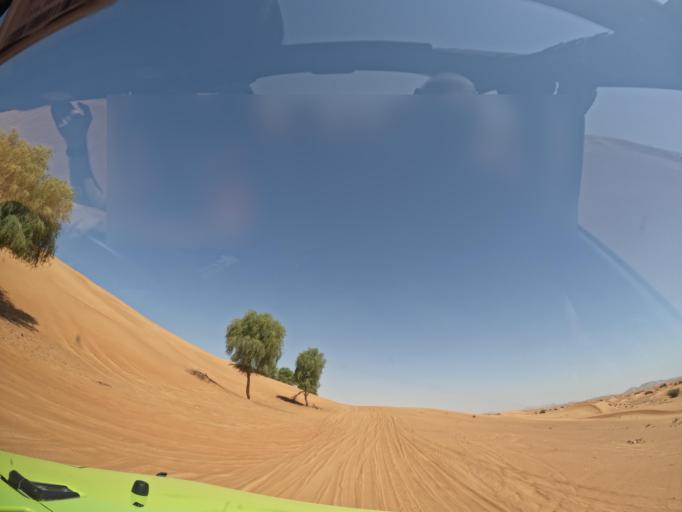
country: AE
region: Ash Shariqah
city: Adh Dhayd
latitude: 24.9740
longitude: 55.7212
